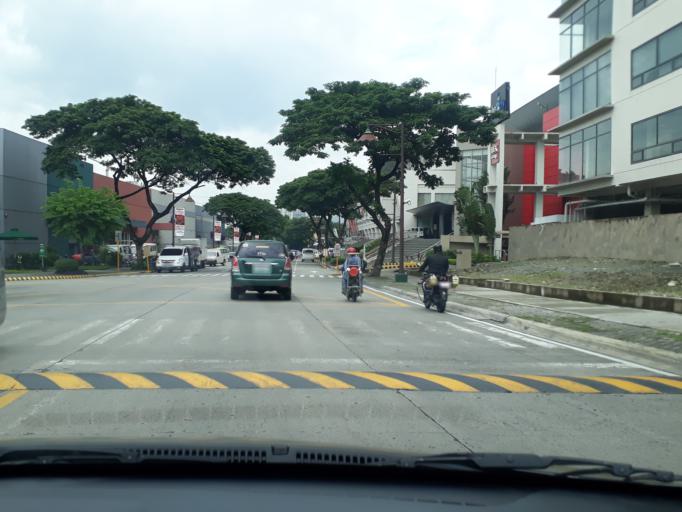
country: PH
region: Metro Manila
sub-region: Pasig
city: Pasig City
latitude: 14.5857
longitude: 121.0770
